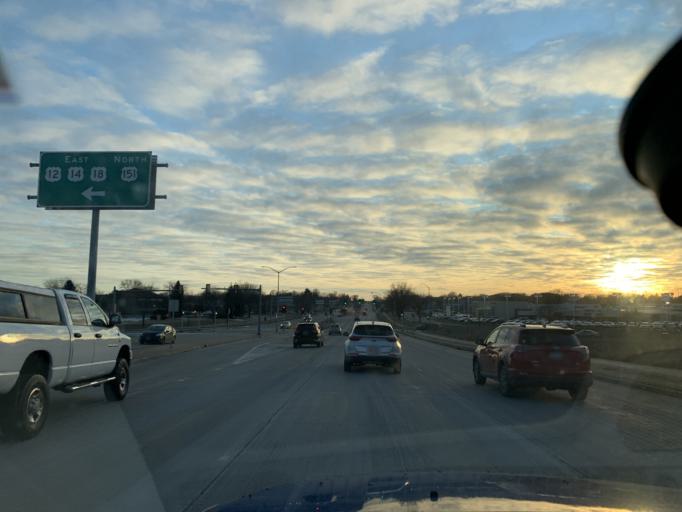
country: US
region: Wisconsin
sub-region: Dane County
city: Madison
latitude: 43.0343
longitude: -89.4072
